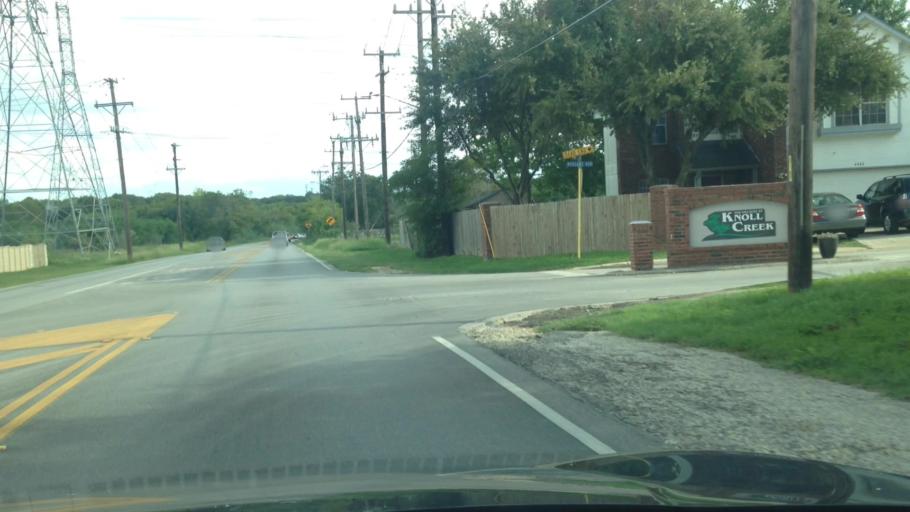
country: US
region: Texas
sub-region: Bexar County
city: Live Oak
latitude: 29.5831
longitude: -98.4041
